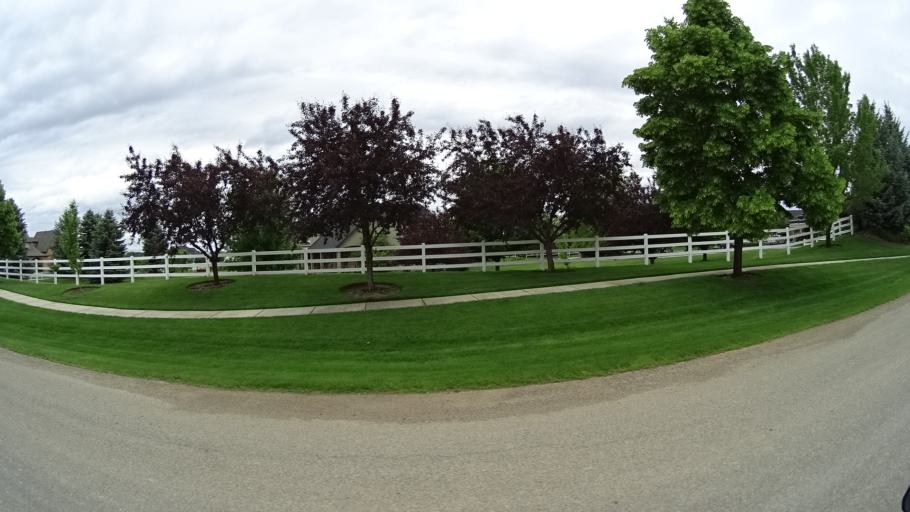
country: US
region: Idaho
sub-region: Ada County
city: Eagle
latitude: 43.7149
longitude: -116.3935
